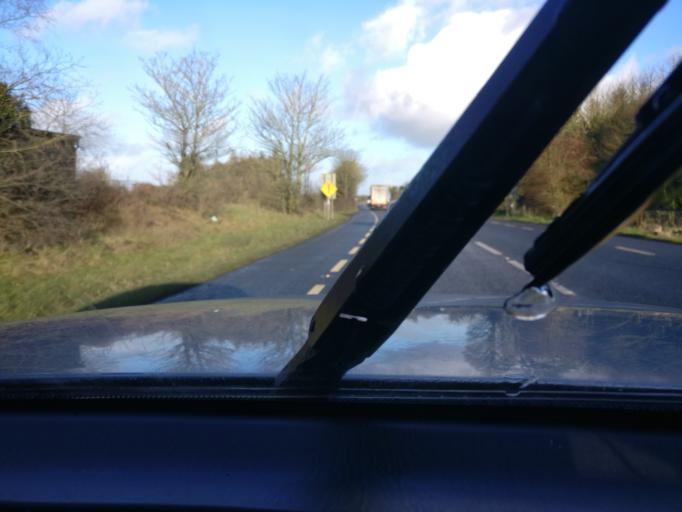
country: IE
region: Leinster
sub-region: An Iarmhi
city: Rathwire
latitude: 53.5885
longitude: -7.1271
